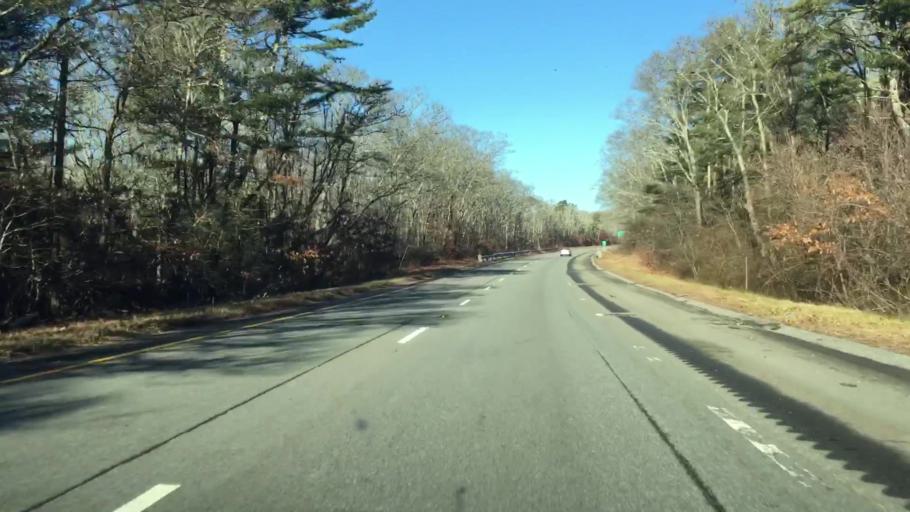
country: US
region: Massachusetts
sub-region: Barnstable County
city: West Falmouth
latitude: 41.5846
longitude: -70.6284
